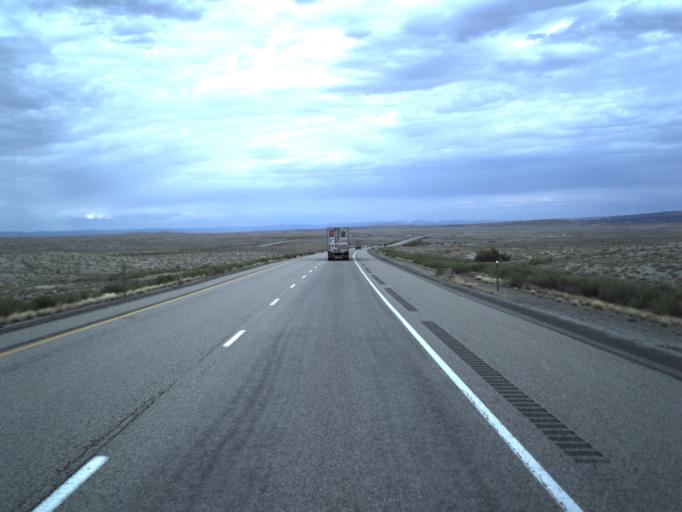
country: US
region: Utah
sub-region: Grand County
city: Moab
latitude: 38.9594
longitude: -109.3806
